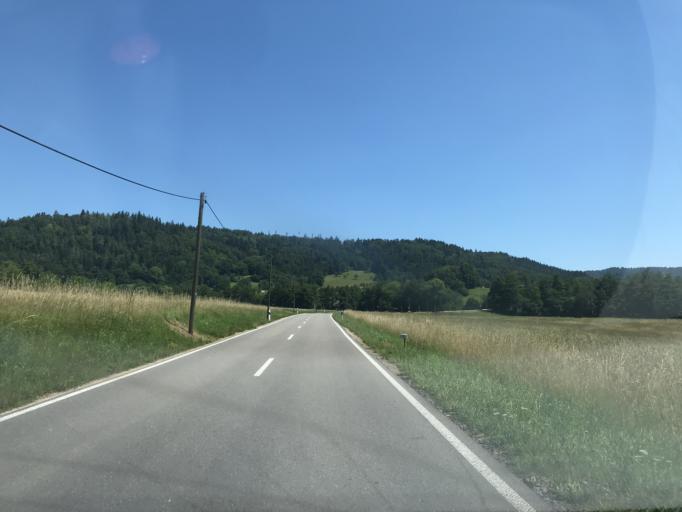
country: DE
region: Baden-Wuerttemberg
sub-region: Freiburg Region
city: Maulburg
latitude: 47.6821
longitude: 7.7697
